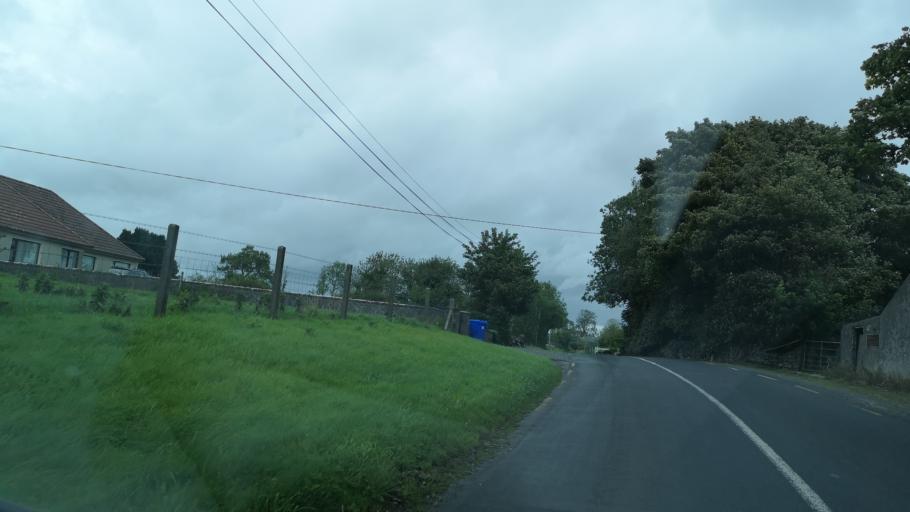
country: IE
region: Connaught
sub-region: County Galway
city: Loughrea
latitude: 53.2846
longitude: -8.5819
